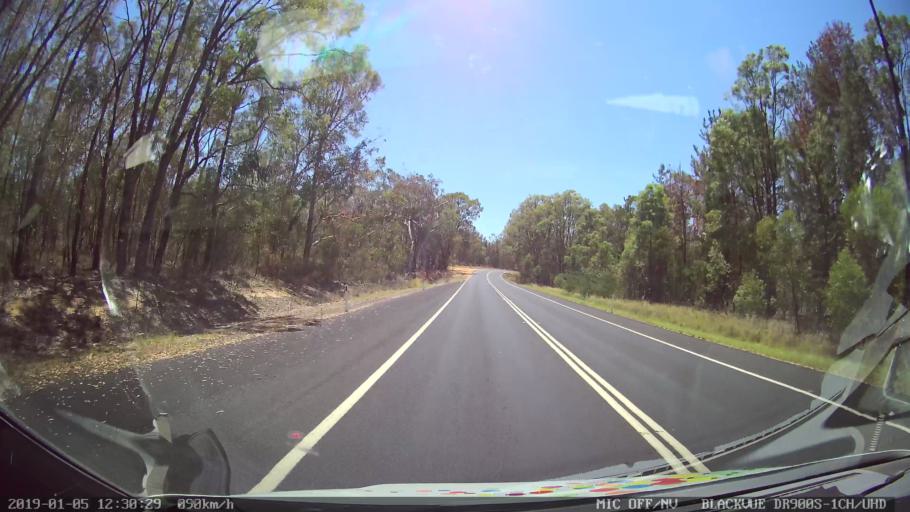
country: AU
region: New South Wales
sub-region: Warrumbungle Shire
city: Coonabarabran
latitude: -31.2274
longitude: 149.3509
